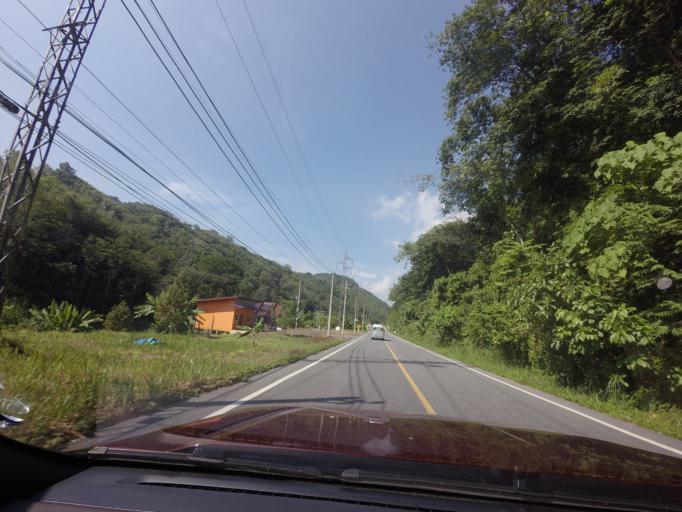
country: TH
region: Yala
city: Betong
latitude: 5.9455
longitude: 101.1900
